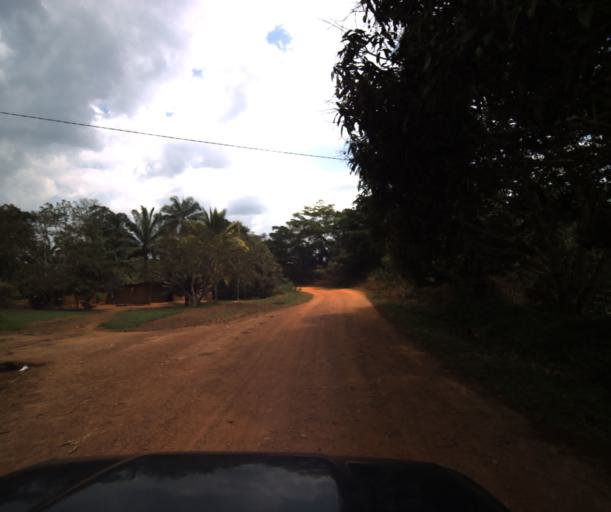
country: CM
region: Centre
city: Akono
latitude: 3.5578
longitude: 11.0881
